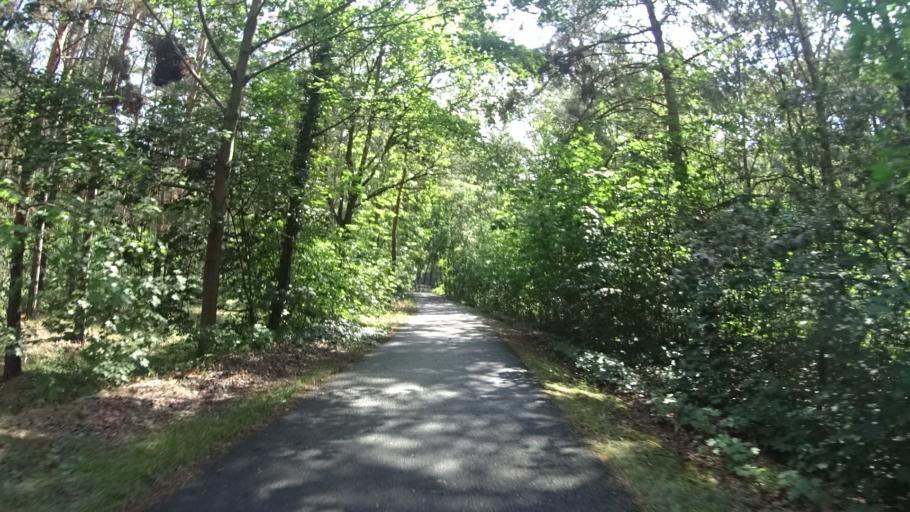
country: DE
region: Brandenburg
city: Guhrow
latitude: 51.8097
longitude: 14.2091
